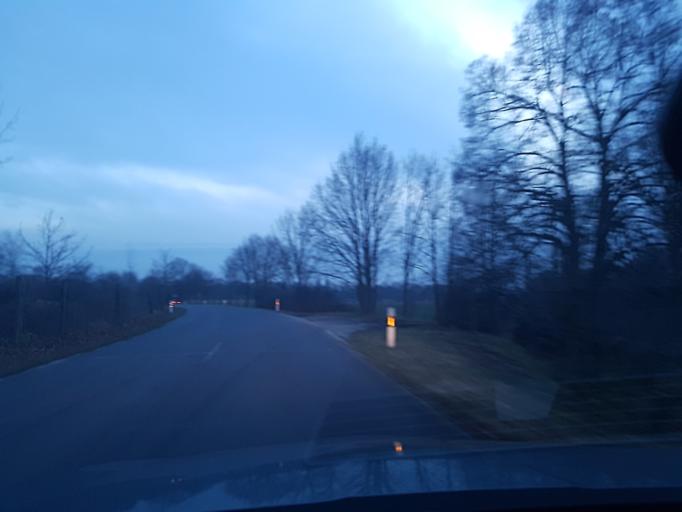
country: DE
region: Brandenburg
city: Ruckersdorf
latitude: 51.6016
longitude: 13.5464
